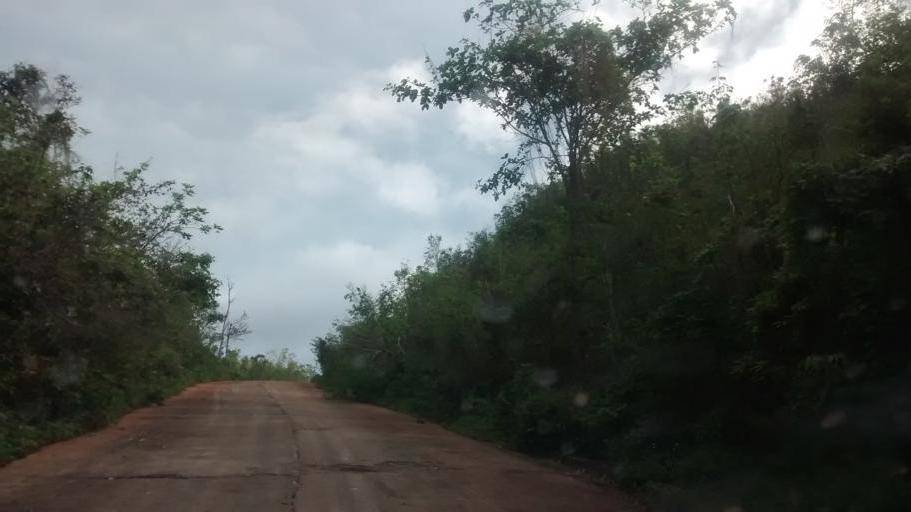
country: HT
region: Grandans
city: Corail
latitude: 18.5085
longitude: -73.7823
